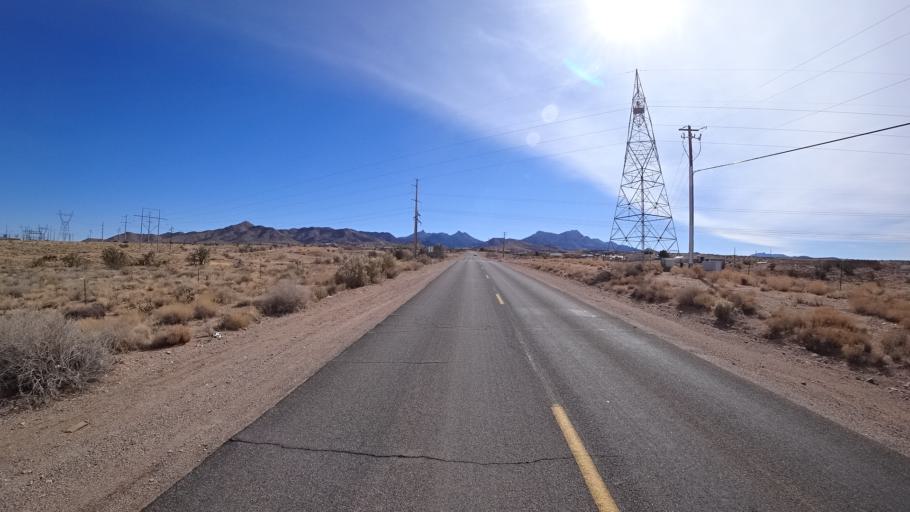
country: US
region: Arizona
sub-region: Mohave County
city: Kingman
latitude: 35.1755
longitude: -113.9879
